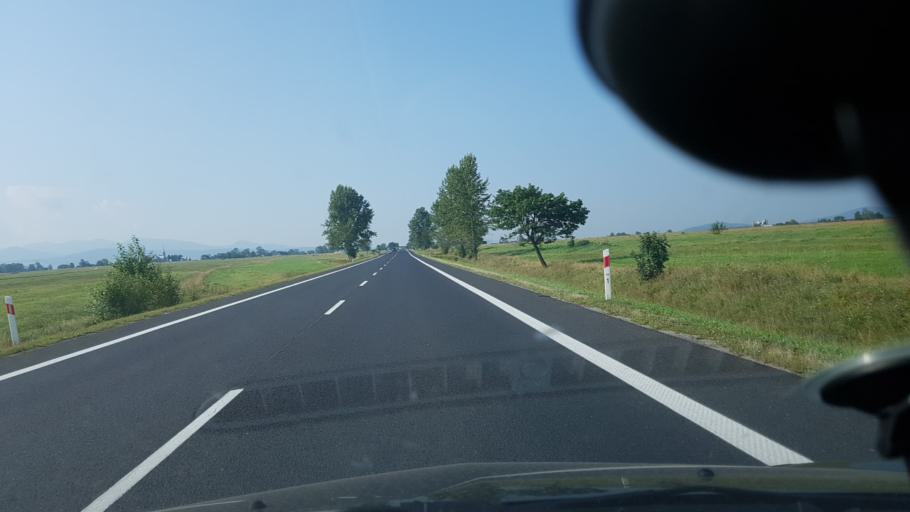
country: PL
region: Lesser Poland Voivodeship
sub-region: Powiat nowotarski
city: Chyzne
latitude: 49.4368
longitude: 19.6801
